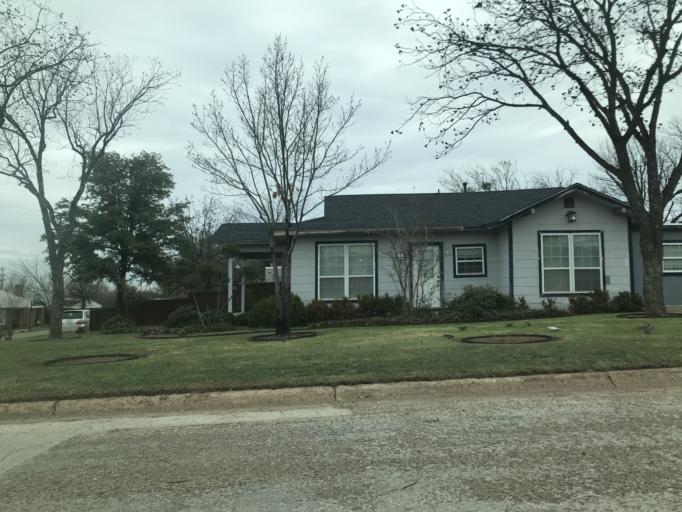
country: US
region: Texas
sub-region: Taylor County
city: Abilene
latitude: 32.4456
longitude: -99.7536
